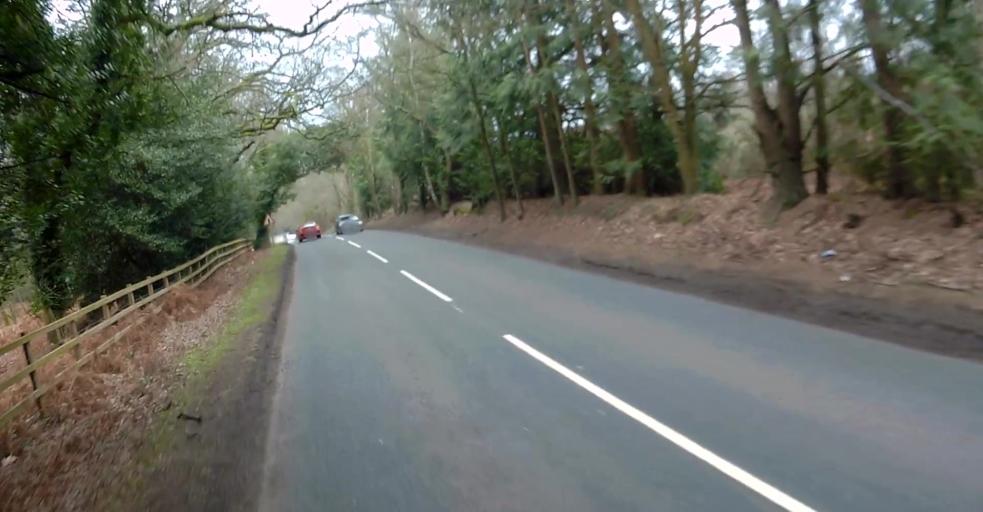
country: GB
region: England
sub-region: Hampshire
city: Eversley
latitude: 51.3460
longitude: -0.9048
